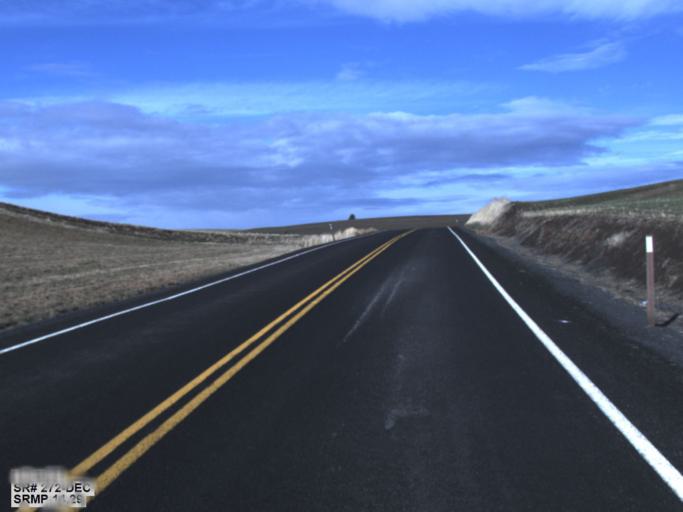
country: US
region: Washington
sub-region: Whitman County
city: Pullman
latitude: 46.9242
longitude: -117.1077
